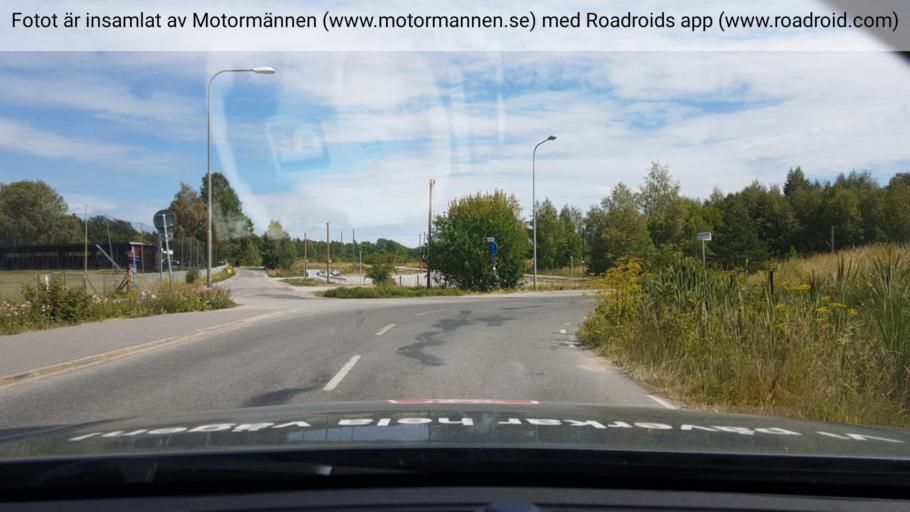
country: SE
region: Stockholm
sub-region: Jarfalla Kommun
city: Jakobsberg
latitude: 59.3890
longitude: 17.7897
